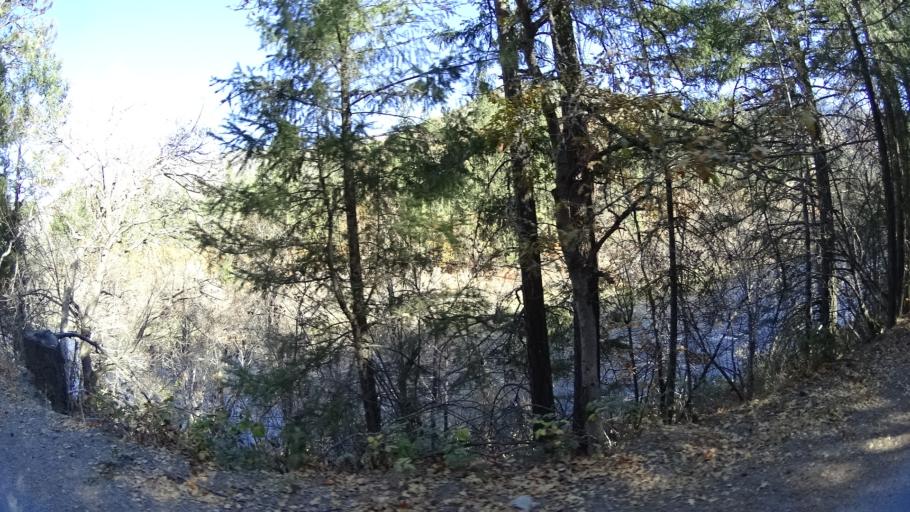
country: US
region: California
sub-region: Siskiyou County
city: Yreka
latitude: 41.8554
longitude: -122.7038
